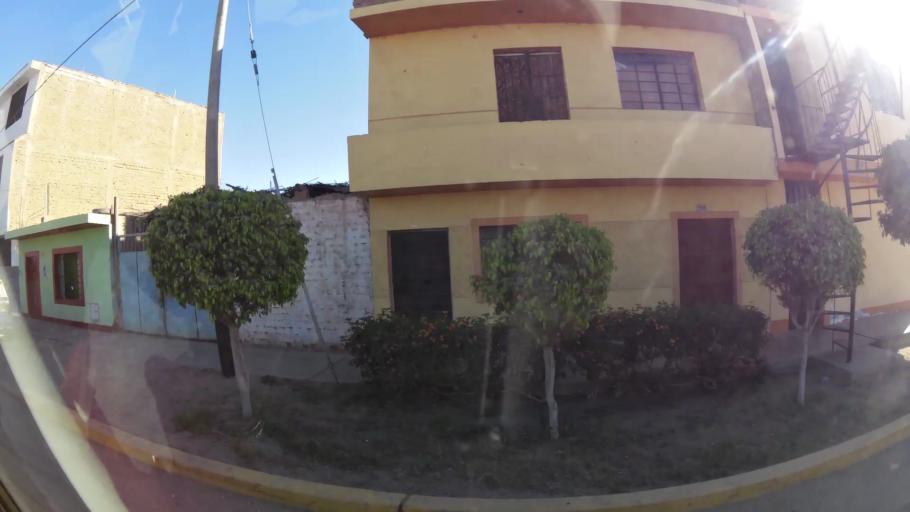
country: PE
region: Ica
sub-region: Provincia de Ica
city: La Tinguina
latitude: -14.0406
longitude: -75.7098
